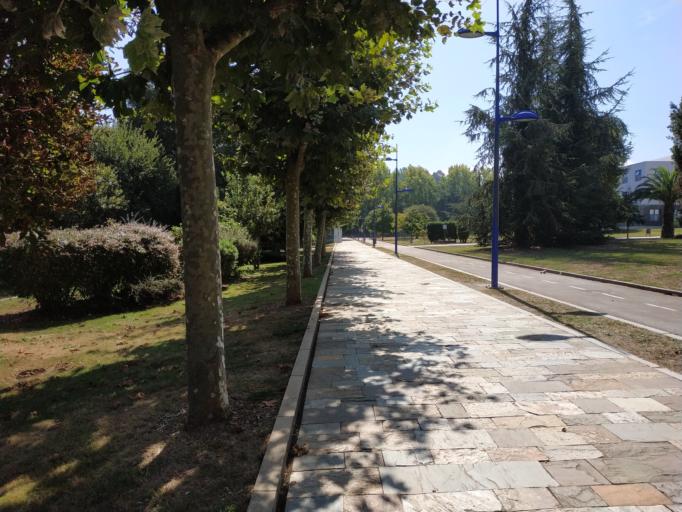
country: ES
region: Galicia
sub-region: Provincia da Coruna
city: Culleredo
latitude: 43.3152
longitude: -8.3725
